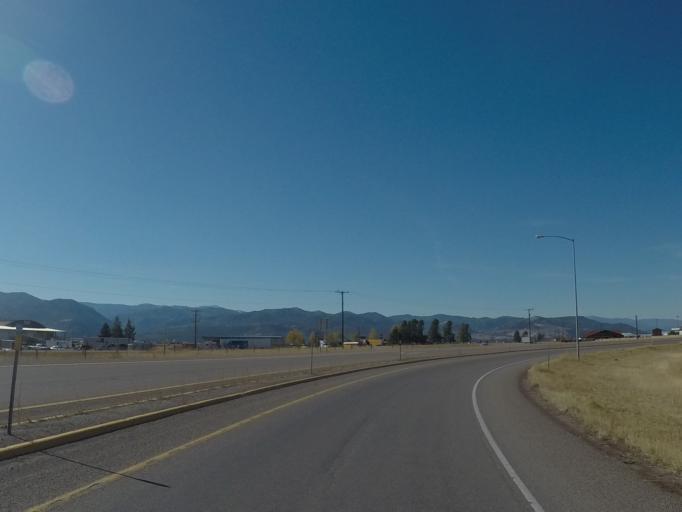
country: US
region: Montana
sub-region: Missoula County
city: Frenchtown
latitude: 46.9493
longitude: -114.1331
